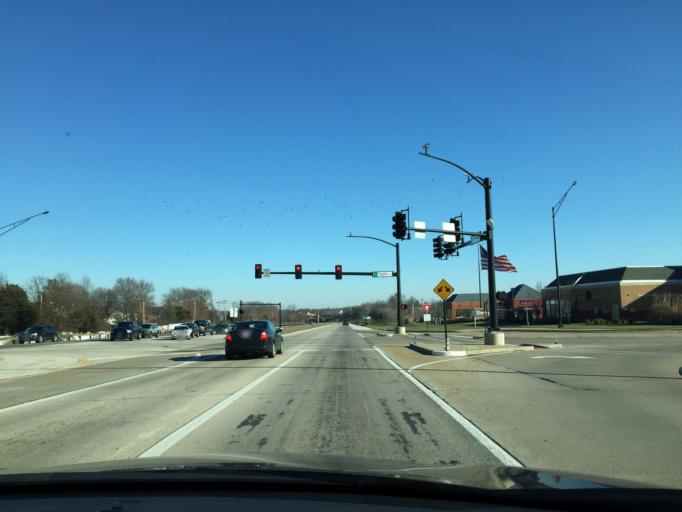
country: US
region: Missouri
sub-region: Saint Louis County
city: Wildwood
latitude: 38.5826
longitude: -90.6281
